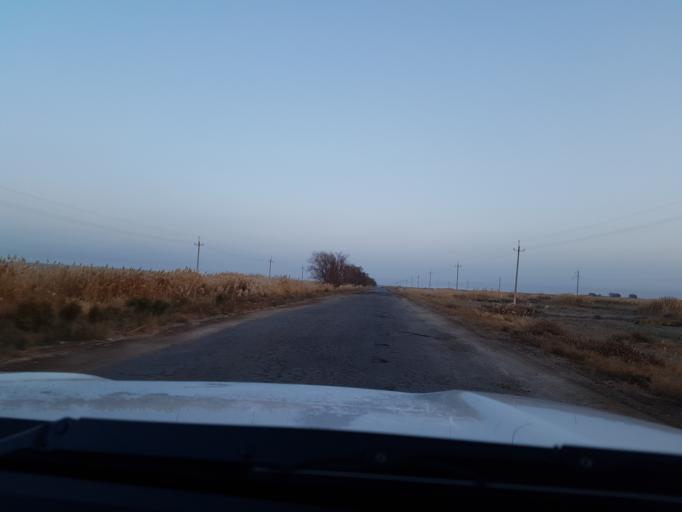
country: TM
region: Dasoguz
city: Koeneuergench
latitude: 41.7642
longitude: 58.6926
